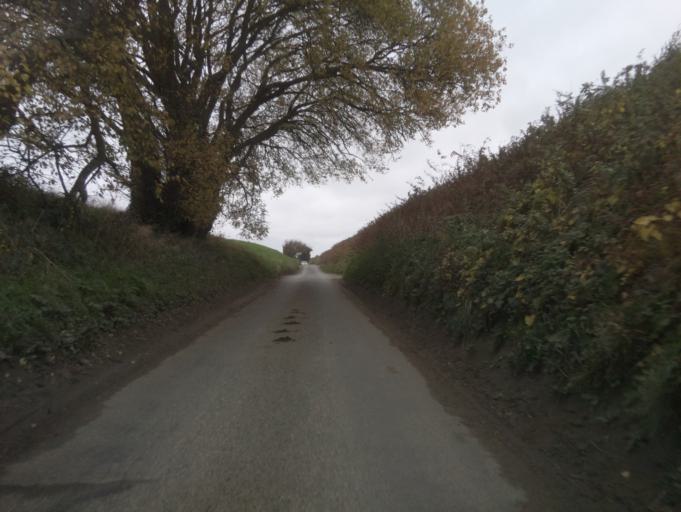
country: GB
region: England
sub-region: Somerset
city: South Petherton
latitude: 50.9429
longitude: -2.8511
